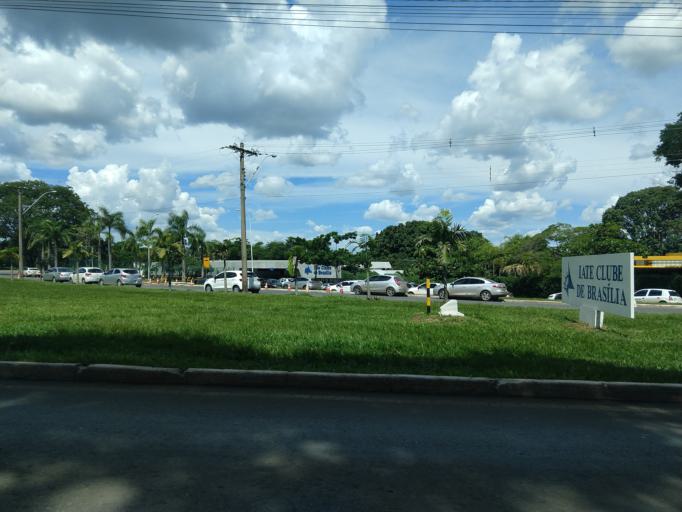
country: BR
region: Federal District
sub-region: Brasilia
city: Brasilia
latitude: -15.7789
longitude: -47.8621
